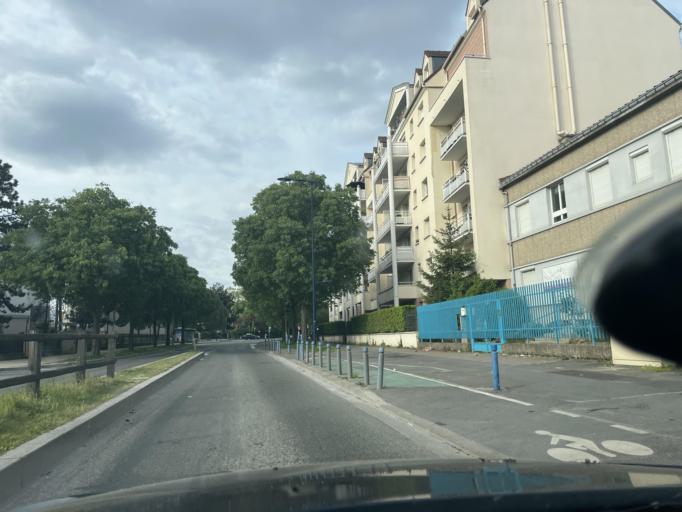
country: FR
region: Ile-de-France
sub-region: Departement de Seine-Saint-Denis
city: Dugny
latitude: 48.9485
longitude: 2.4142
